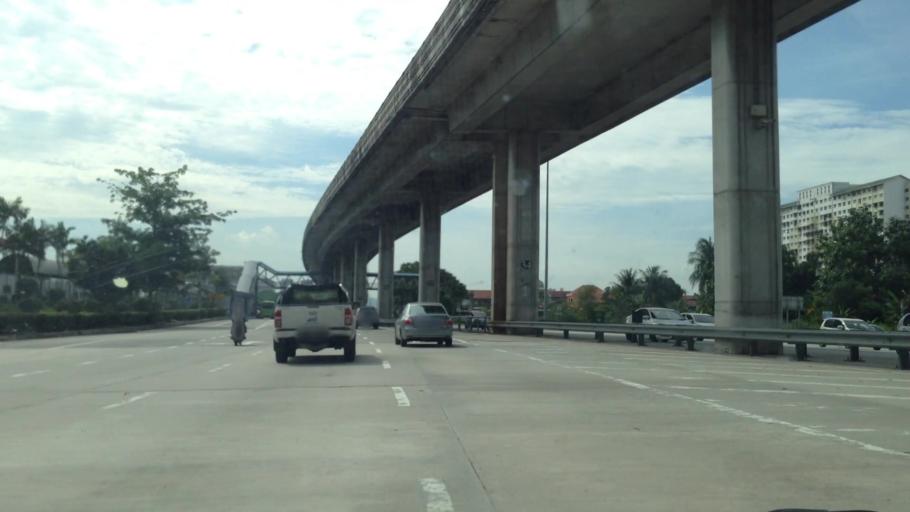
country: MY
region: Selangor
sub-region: Petaling
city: Petaling Jaya
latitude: 3.0843
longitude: 101.6318
